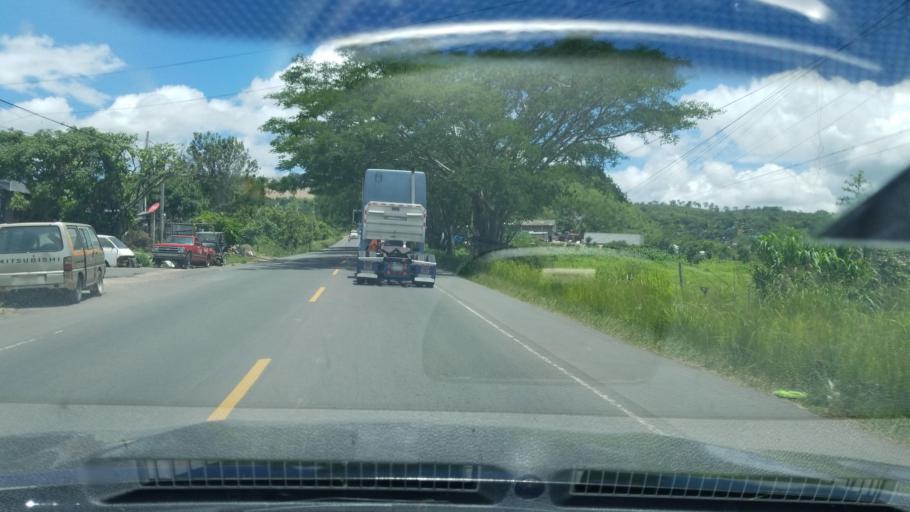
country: HN
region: Francisco Morazan
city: Rio Abajo
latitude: 14.1506
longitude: -87.2083
